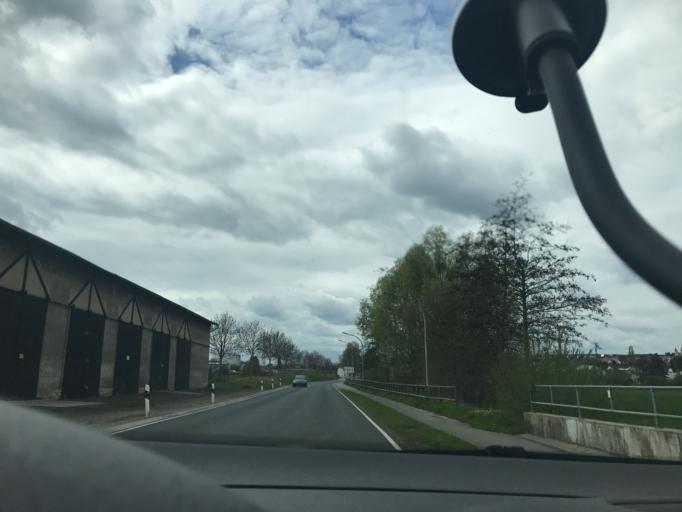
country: DE
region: Lower Saxony
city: Schoningen
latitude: 52.1291
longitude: 10.9789
